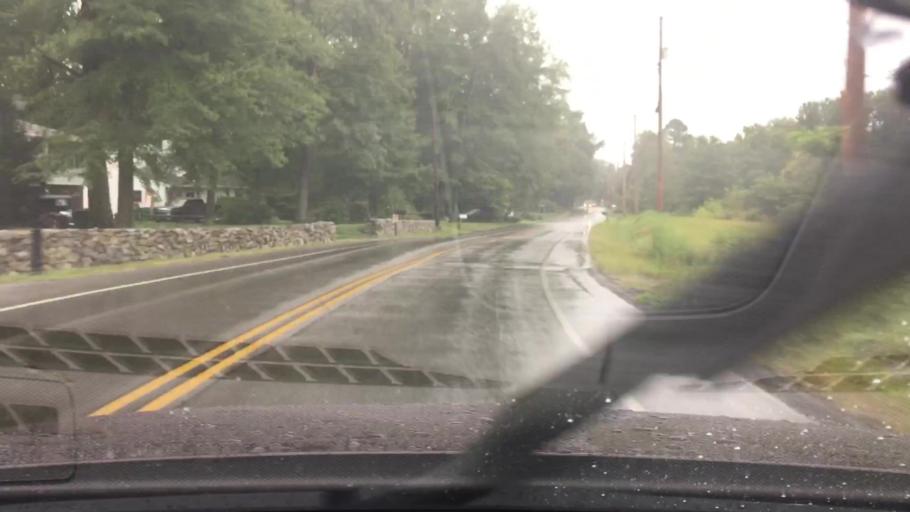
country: US
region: New York
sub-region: Dutchess County
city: Spackenkill
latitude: 41.6276
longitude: -73.9084
